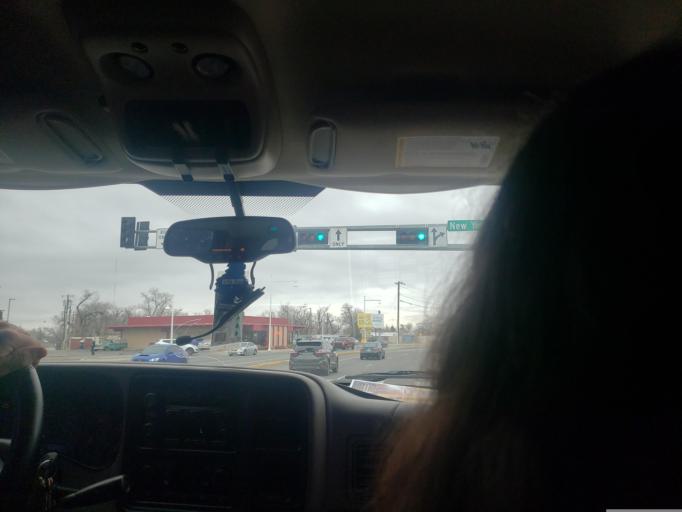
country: US
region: New Mexico
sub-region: Bernalillo County
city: Albuquerque
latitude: 35.0940
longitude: -106.6775
